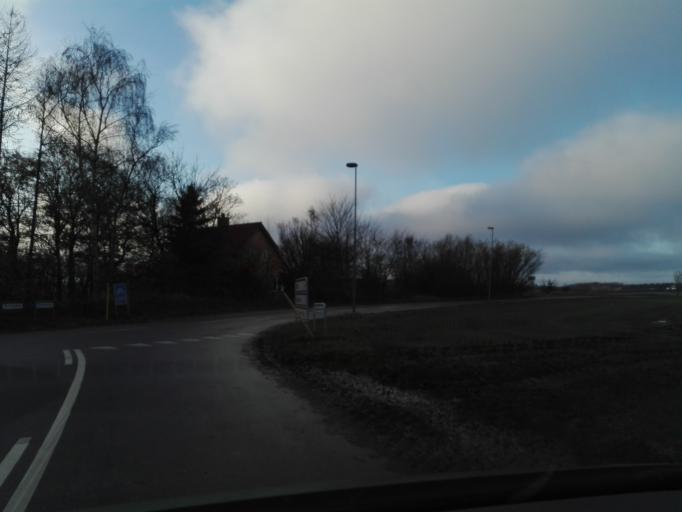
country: DK
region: Central Jutland
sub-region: Arhus Kommune
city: Solbjerg
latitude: 56.0213
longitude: 10.0743
